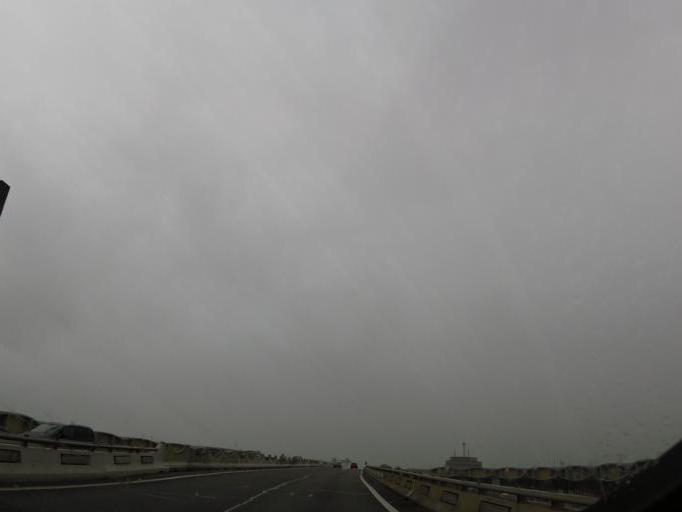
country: FR
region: Ile-de-France
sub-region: Departement de Seine-et-Marne
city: Mitry-Mory
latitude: 49.0040
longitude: 2.5691
